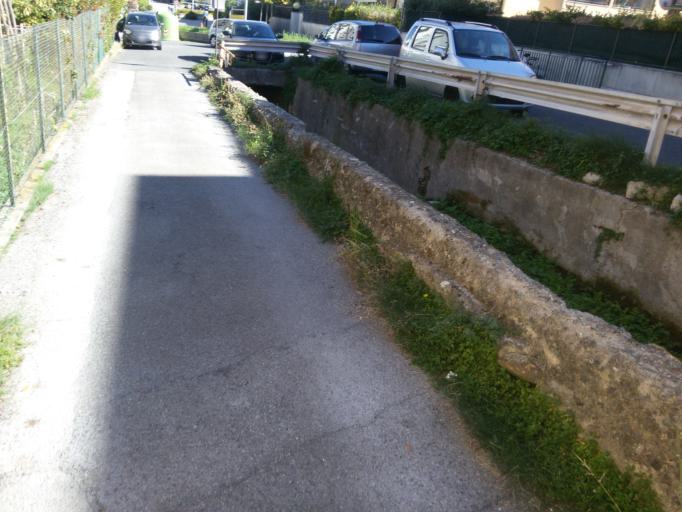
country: IT
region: Liguria
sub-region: Provincia di Genova
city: Chiavari
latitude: 44.3239
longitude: 9.3201
